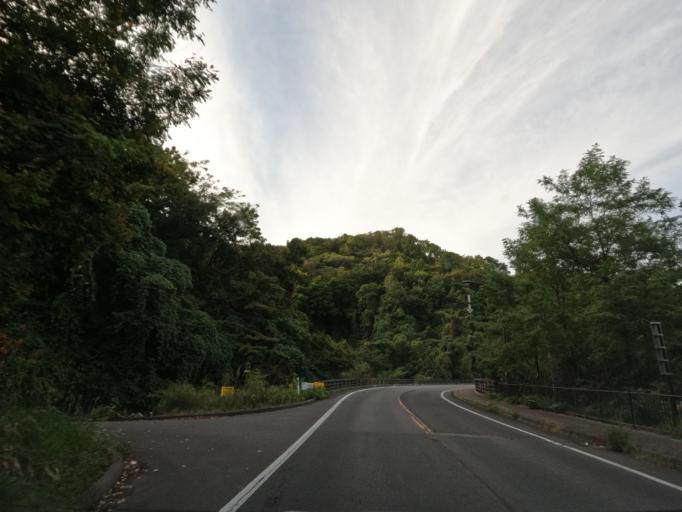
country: JP
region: Hokkaido
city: Date
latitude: 42.5261
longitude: 140.8618
